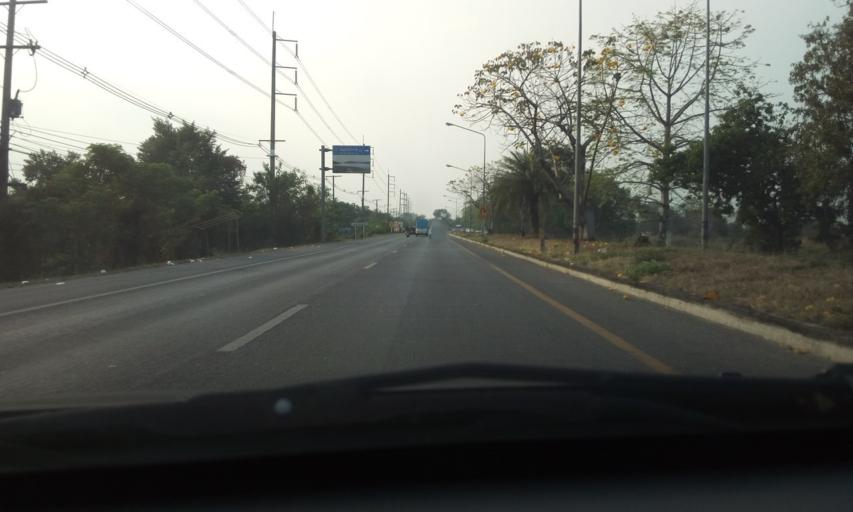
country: TH
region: Nakhon Nayok
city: Nakhon Nayok
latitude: 14.2121
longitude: 101.1755
